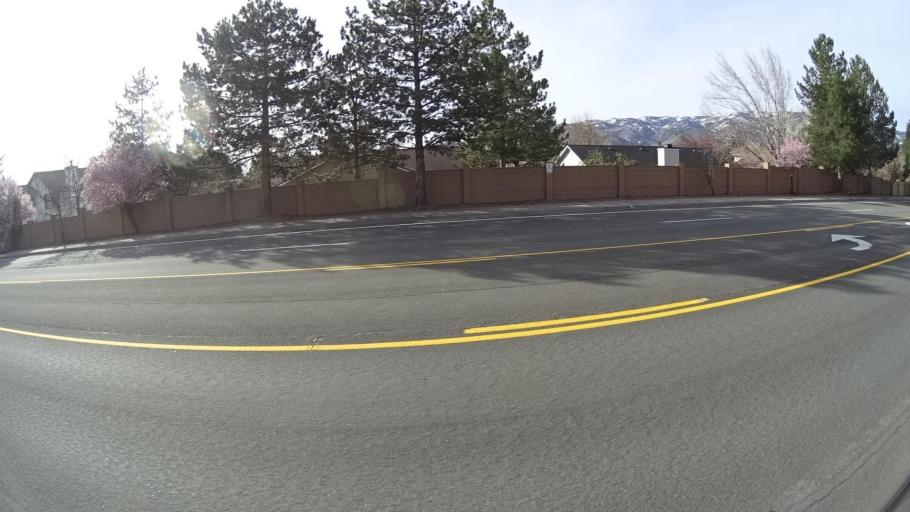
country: US
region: Nevada
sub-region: Washoe County
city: Mogul
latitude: 39.5245
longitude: -119.8979
